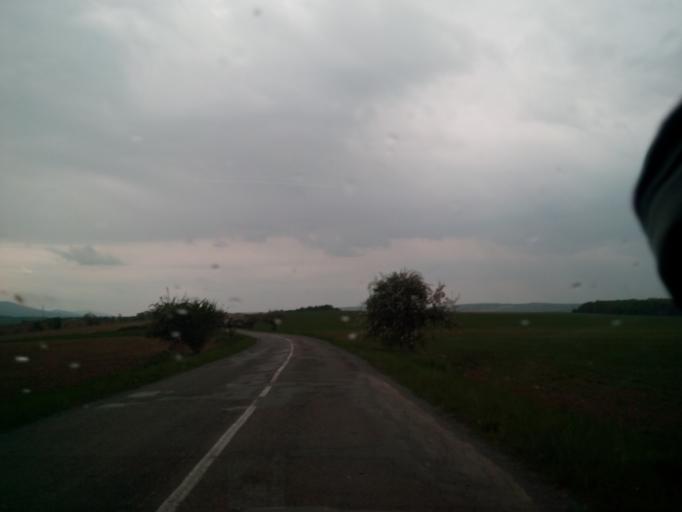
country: SK
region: Kosicky
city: Secovce
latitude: 48.7688
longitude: 21.4707
